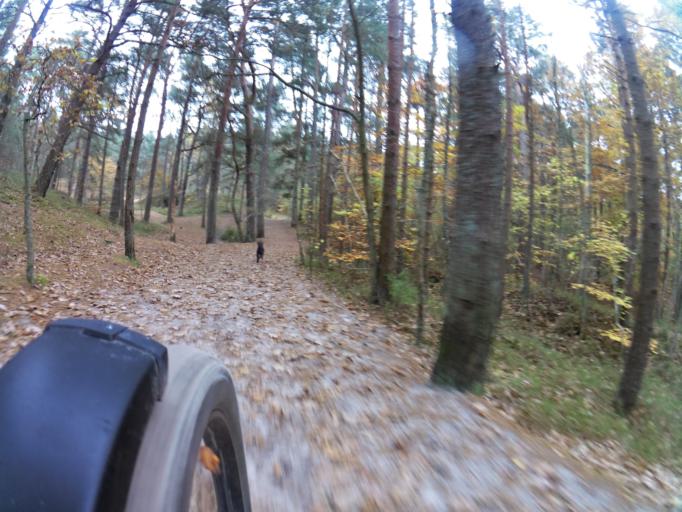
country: PL
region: Pomeranian Voivodeship
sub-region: Powiat pucki
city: Krokowa
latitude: 54.8309
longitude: 18.1426
